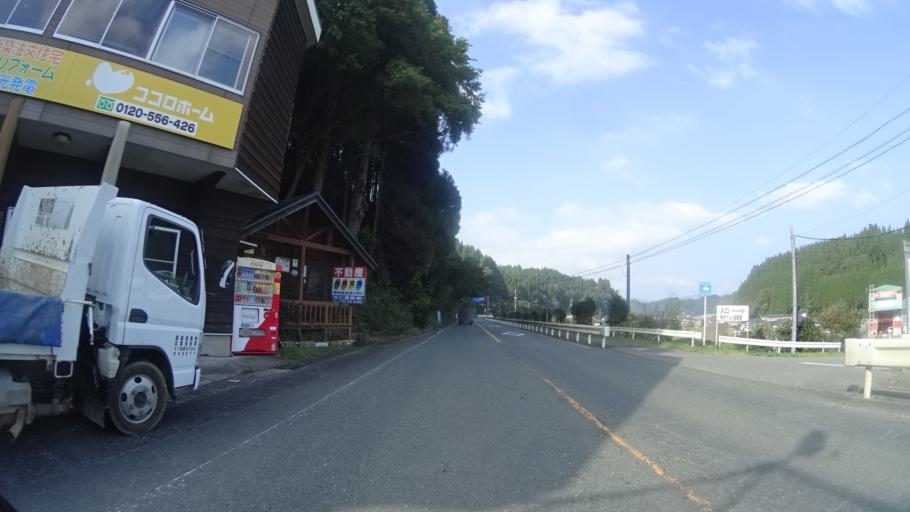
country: JP
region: Kumamoto
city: Aso
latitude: 33.0910
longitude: 131.0672
